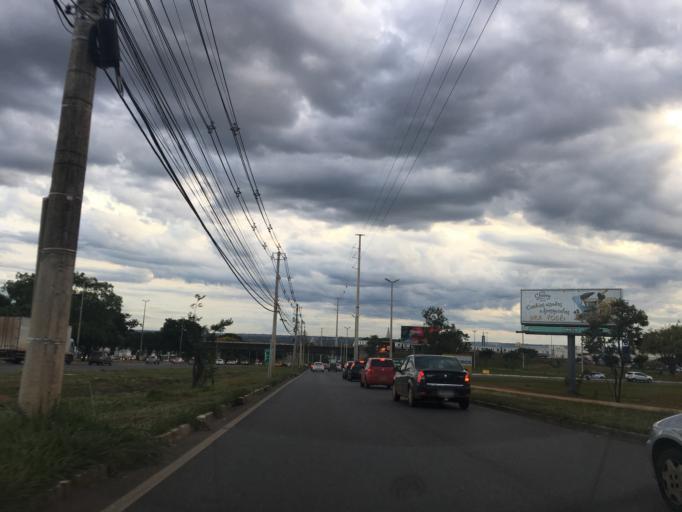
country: BR
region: Federal District
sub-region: Brasilia
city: Brasilia
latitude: -15.8298
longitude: -47.9520
